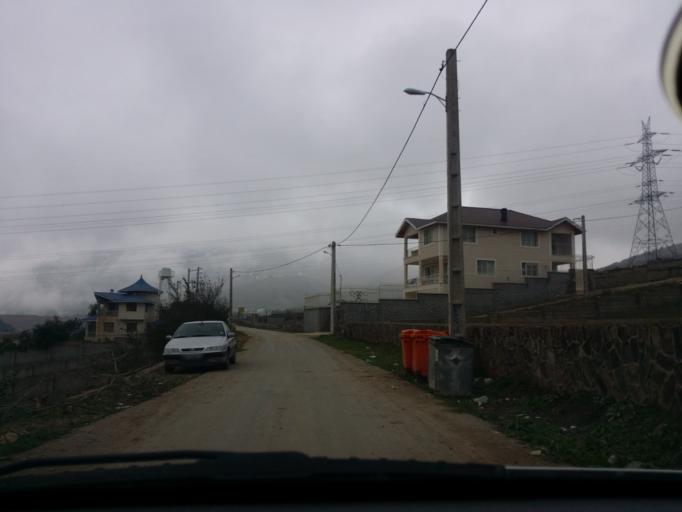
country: IR
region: Mazandaran
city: Chalus
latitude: 36.5122
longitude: 51.2292
